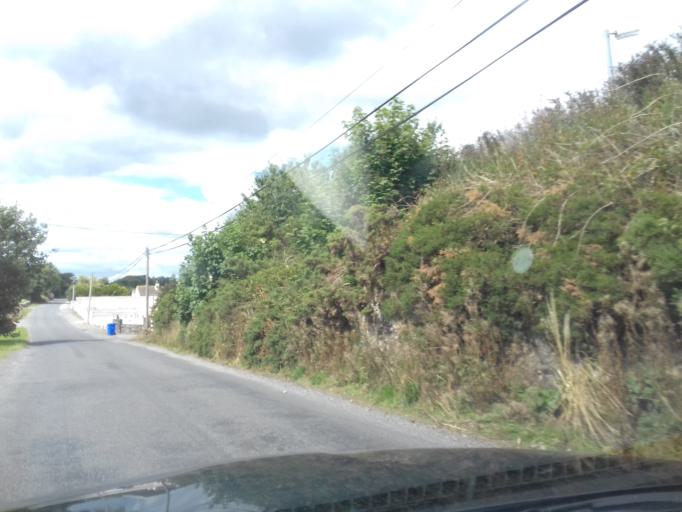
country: IE
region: Munster
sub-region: Waterford
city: Portlaw
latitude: 52.1758
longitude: -7.2856
